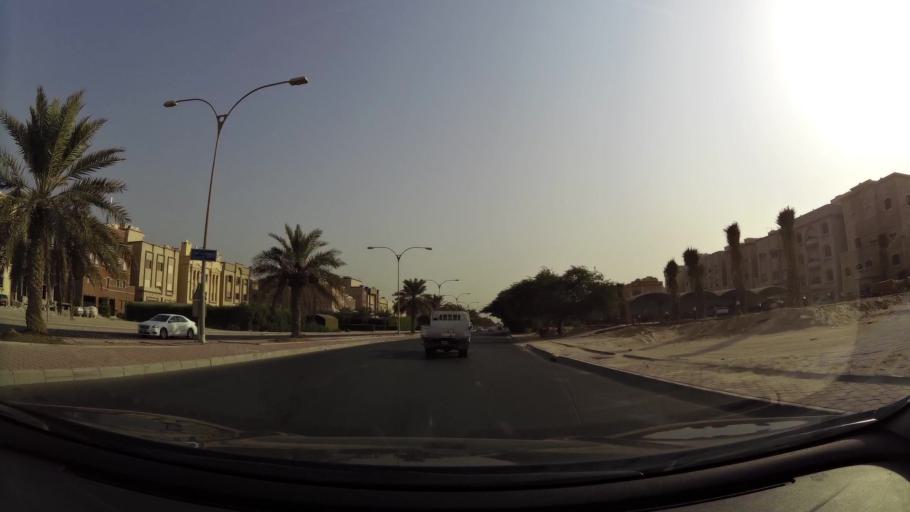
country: KW
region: Al Ahmadi
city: Ar Riqqah
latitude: 29.1261
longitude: 48.1044
